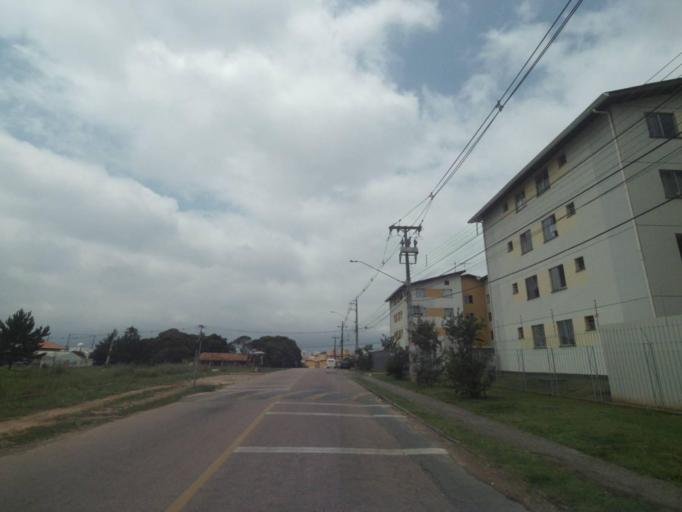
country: BR
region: Parana
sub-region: Curitiba
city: Curitiba
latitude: -25.4897
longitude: -49.3500
